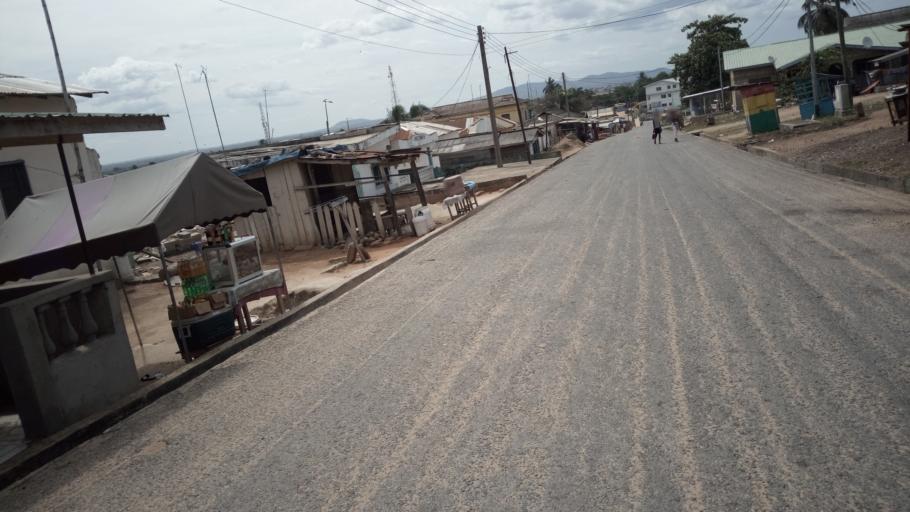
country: GH
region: Central
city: Winneba
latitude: 5.3476
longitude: -0.6233
